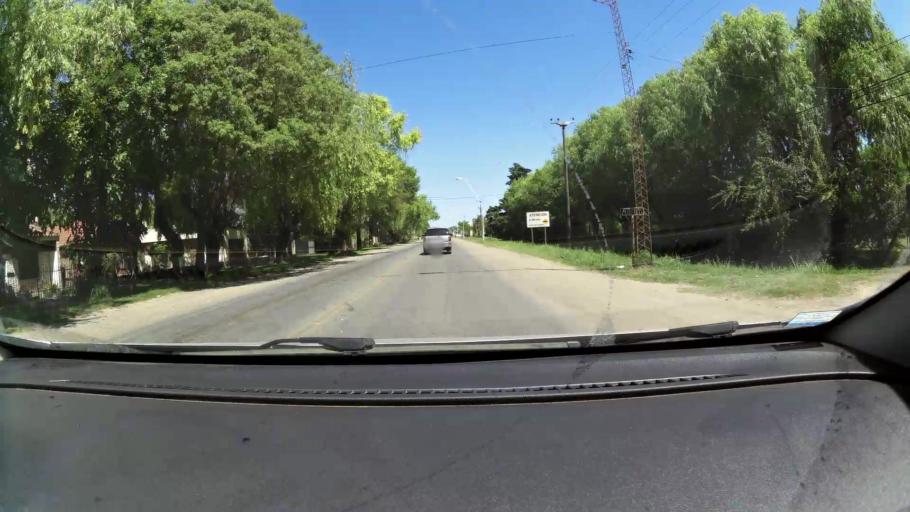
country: AR
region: Santa Fe
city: Esperanza
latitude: -31.4397
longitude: -60.9419
